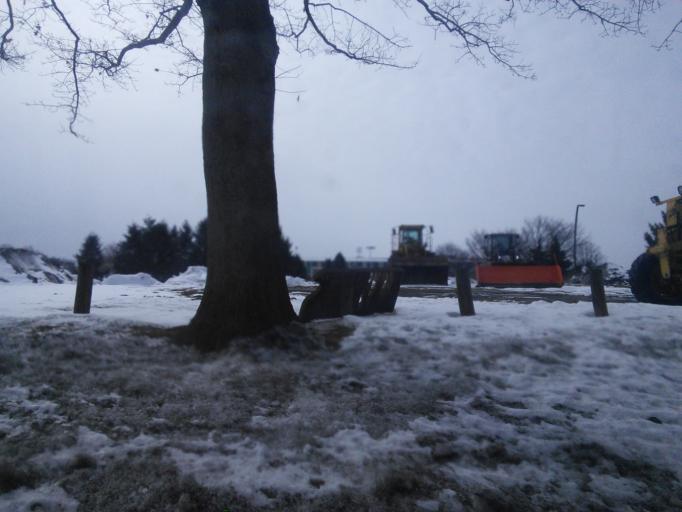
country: US
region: Pennsylvania
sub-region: Centre County
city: State College
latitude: 40.8096
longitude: -77.8509
